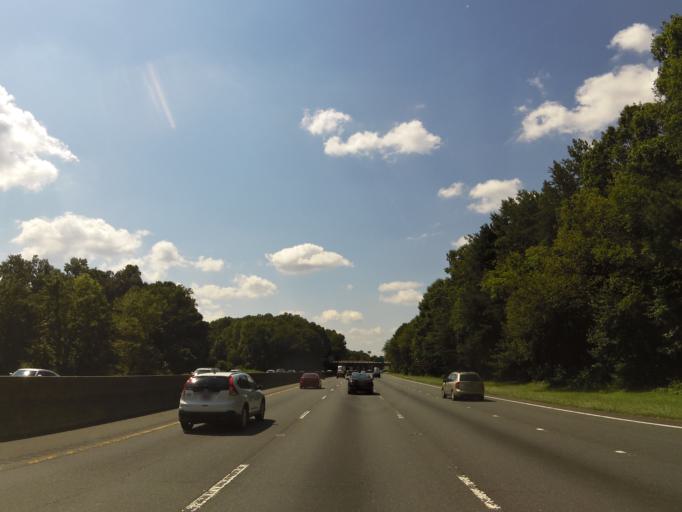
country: US
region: North Carolina
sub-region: Gaston County
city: Ranlo
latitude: 35.2659
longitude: -81.1394
